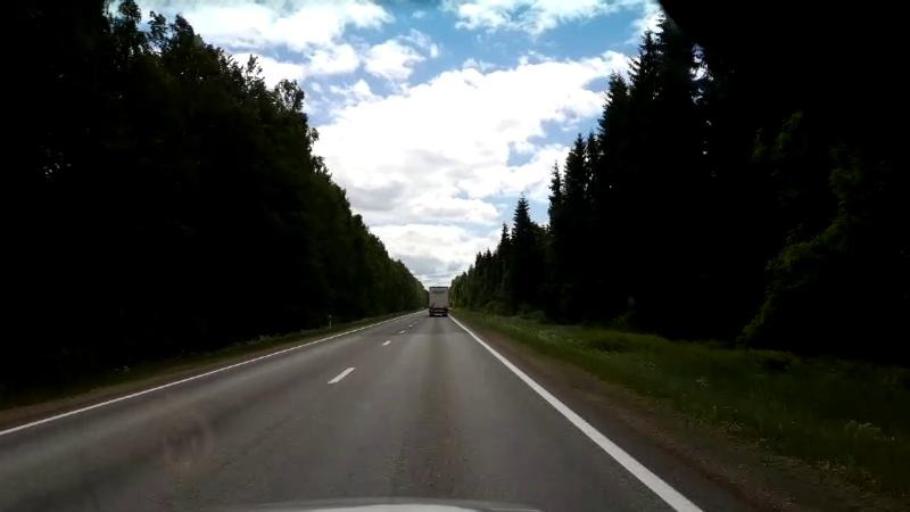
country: LV
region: Salacgrivas
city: Salacgriva
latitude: 57.5978
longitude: 24.4118
